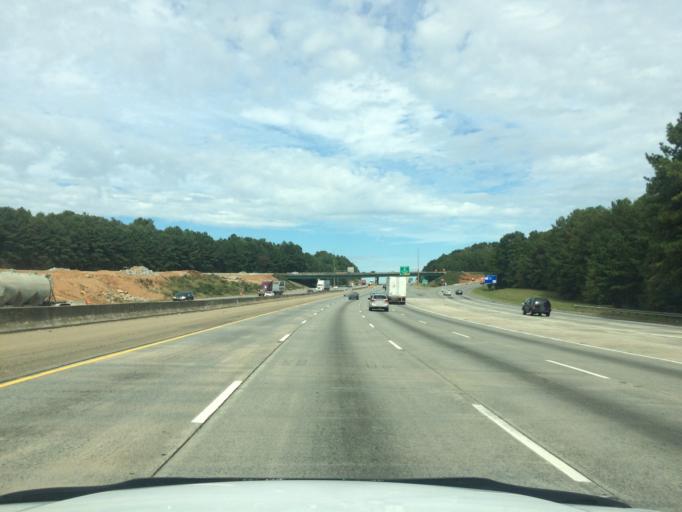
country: US
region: Georgia
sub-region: Cobb County
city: Marietta
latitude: 33.9969
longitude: -84.5599
